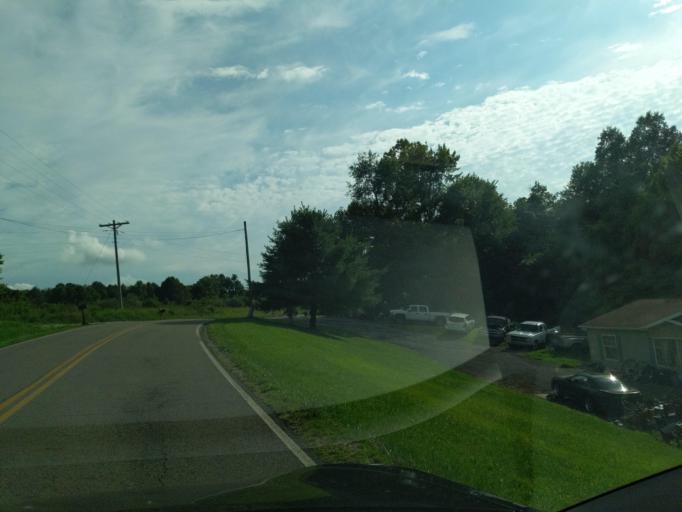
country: US
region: Ohio
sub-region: Fairfield County
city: Lancaster
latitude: 39.5502
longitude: -82.6285
